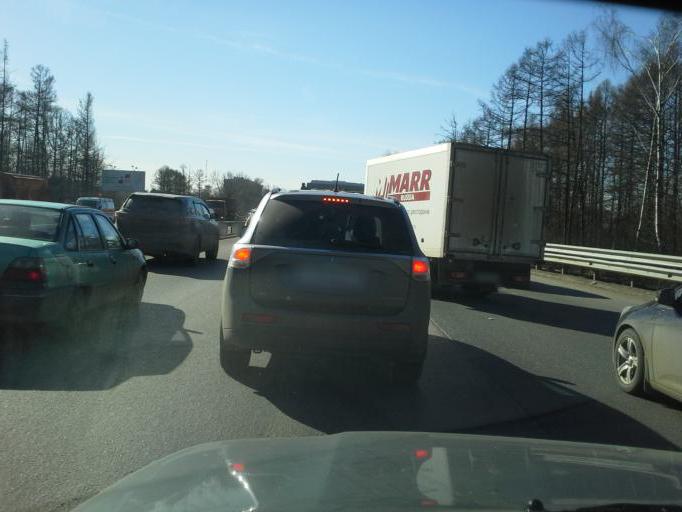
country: RU
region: Moscow
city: Novo-Peredelkino
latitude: 55.6849
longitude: 37.3278
